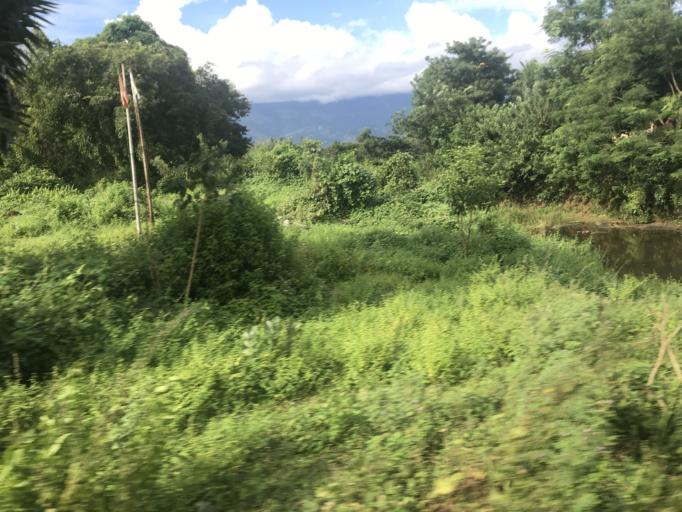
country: IN
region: Kerala
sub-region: Palakkad district
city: Palakkad
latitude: 10.8163
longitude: 76.6905
